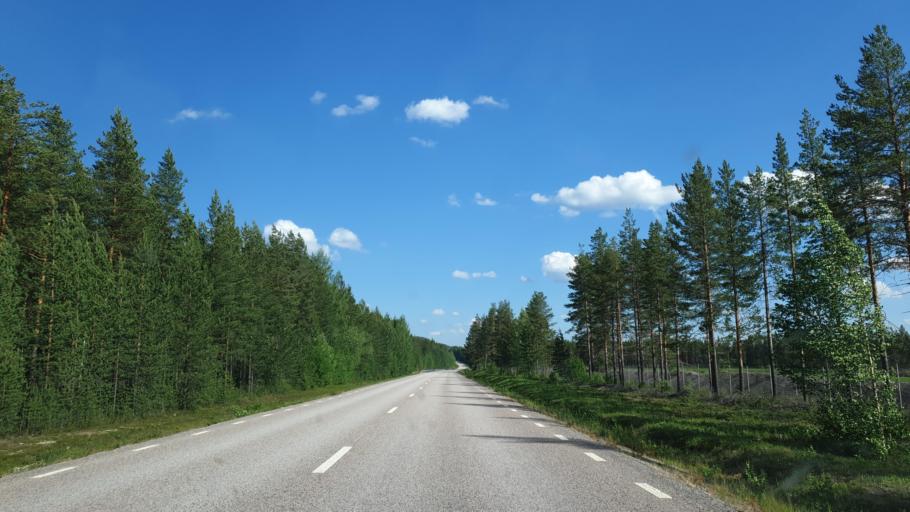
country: SE
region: Norrbotten
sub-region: Alvsbyns Kommun
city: AElvsbyn
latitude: 65.8092
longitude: 20.6027
